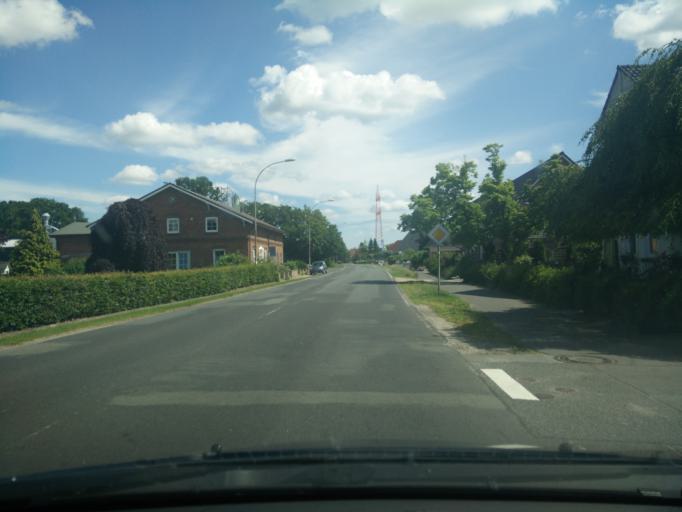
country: DE
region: Schleswig-Holstein
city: Prisdorf
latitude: 53.6838
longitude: 9.7324
